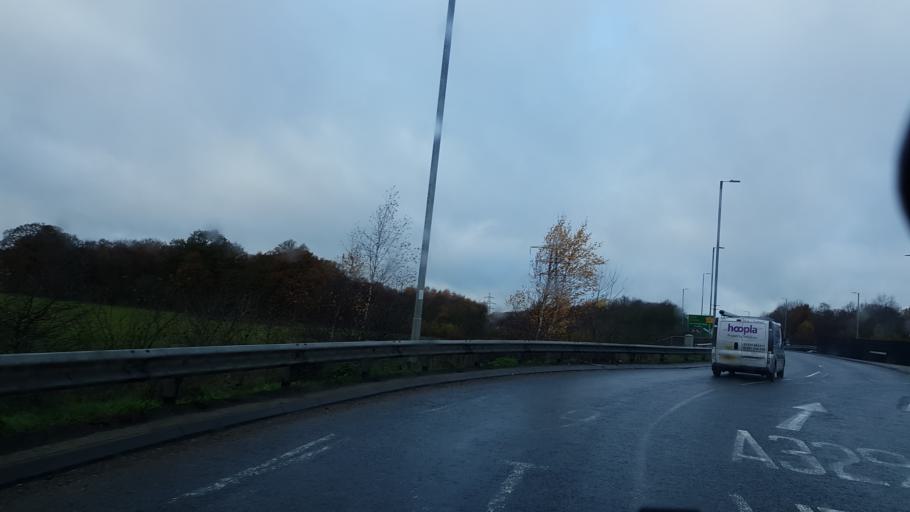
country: GB
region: England
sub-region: Bracknell Forest
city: Binfield
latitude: 51.4093
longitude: -0.7871
